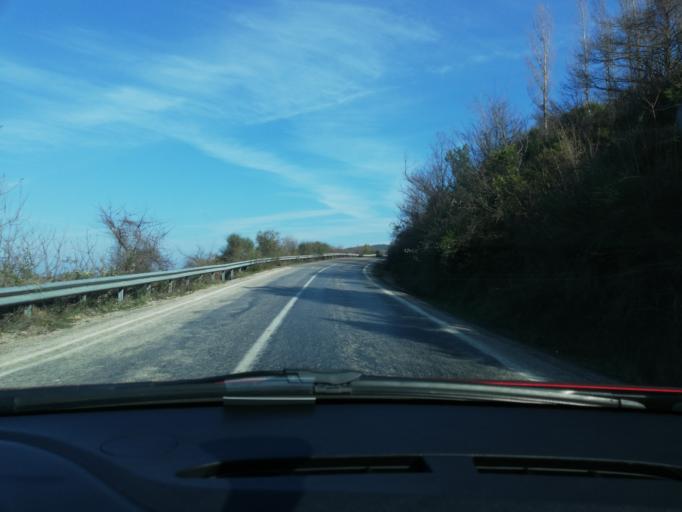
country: TR
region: Bartin
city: Kurucasile
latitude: 41.8468
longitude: 32.7425
